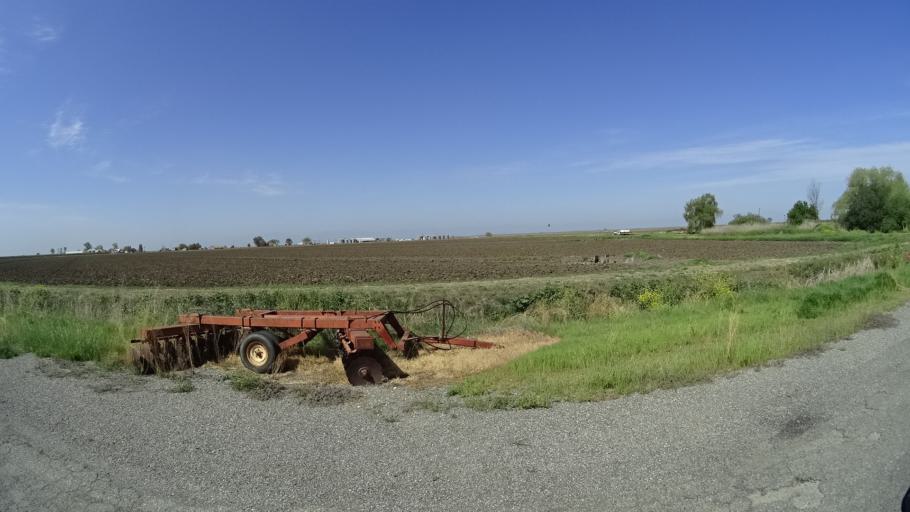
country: US
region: California
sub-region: Glenn County
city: Hamilton City
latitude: 39.6210
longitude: -122.0555
